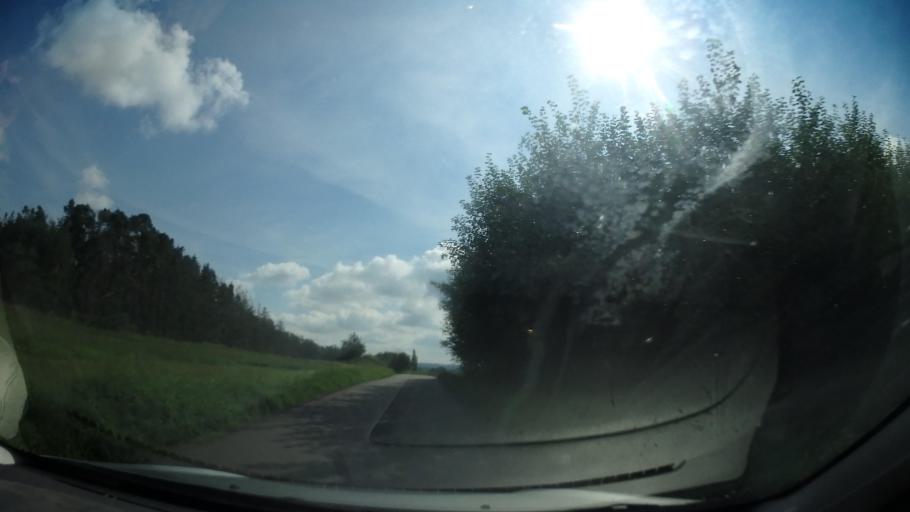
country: CZ
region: Central Bohemia
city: Krasna Hora nad Vltavou
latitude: 49.6878
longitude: 14.3206
